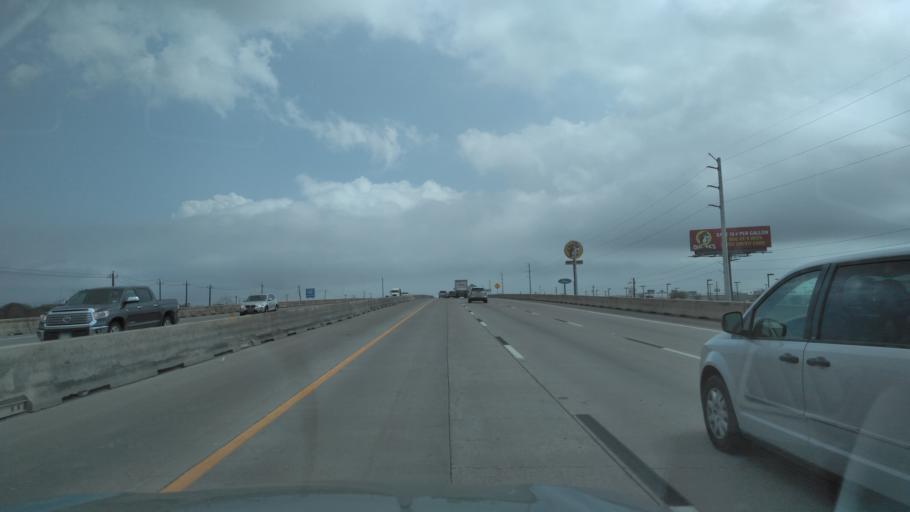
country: US
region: Texas
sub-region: Harris County
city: Highlands
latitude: 29.8017
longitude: -95.0007
